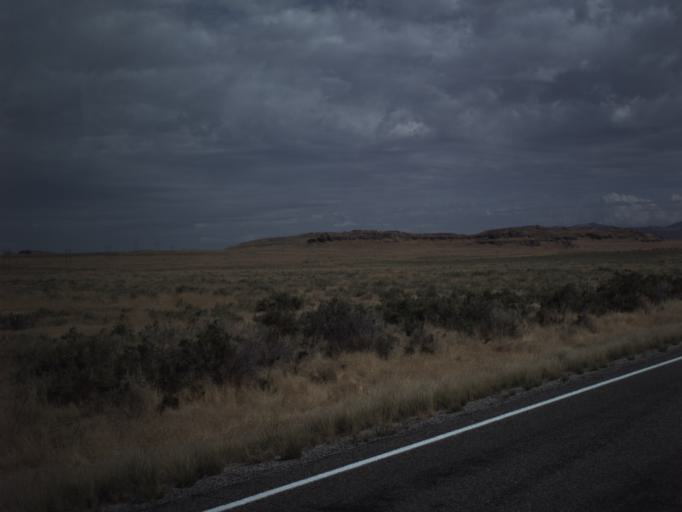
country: US
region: Utah
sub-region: Tooele County
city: Wendover
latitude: 41.4153
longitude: -113.9184
